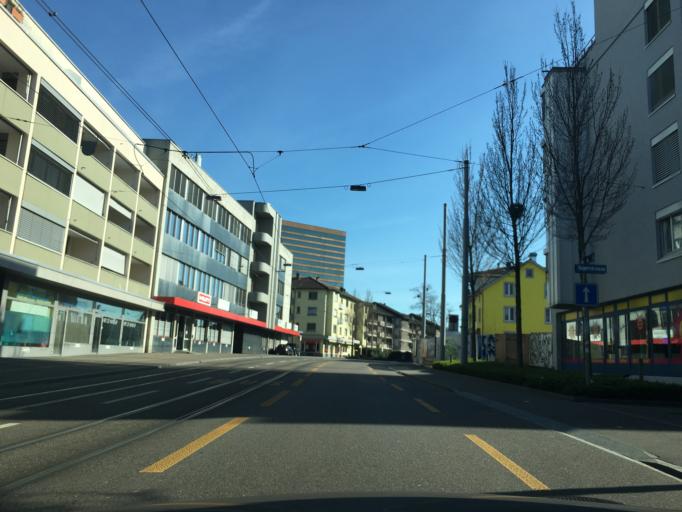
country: CH
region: Zurich
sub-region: Bezirk Zuerich
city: Zuerich (Kreis 11) / Seebach
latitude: 47.4158
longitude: 8.5452
